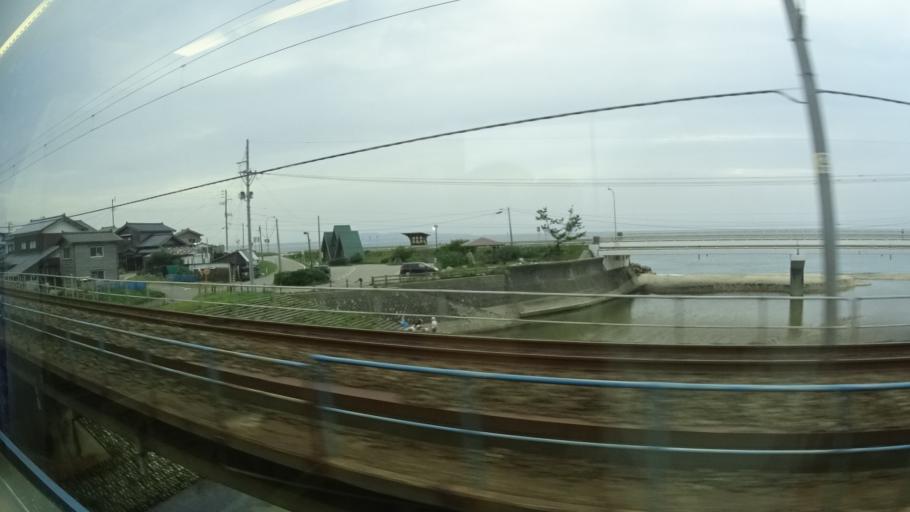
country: JP
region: Niigata
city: Murakami
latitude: 38.4530
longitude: 139.4953
